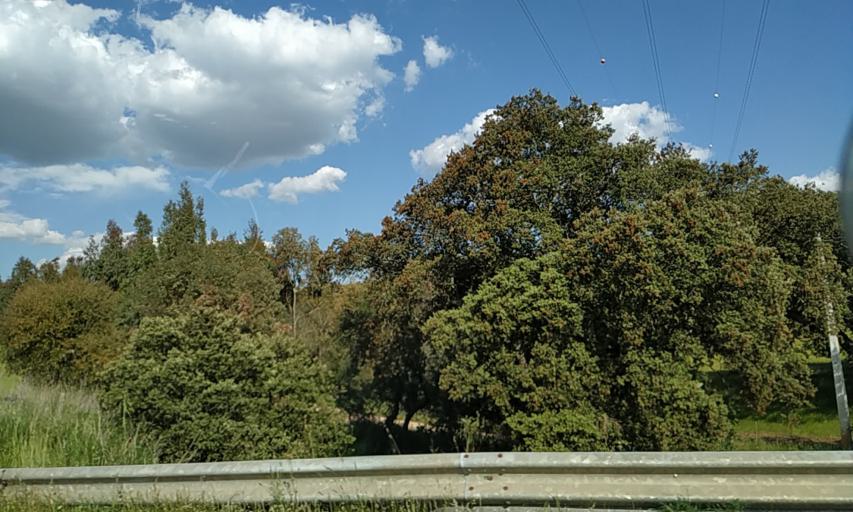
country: PT
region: Evora
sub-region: Estremoz
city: Estremoz
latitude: 38.8819
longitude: -7.5589
